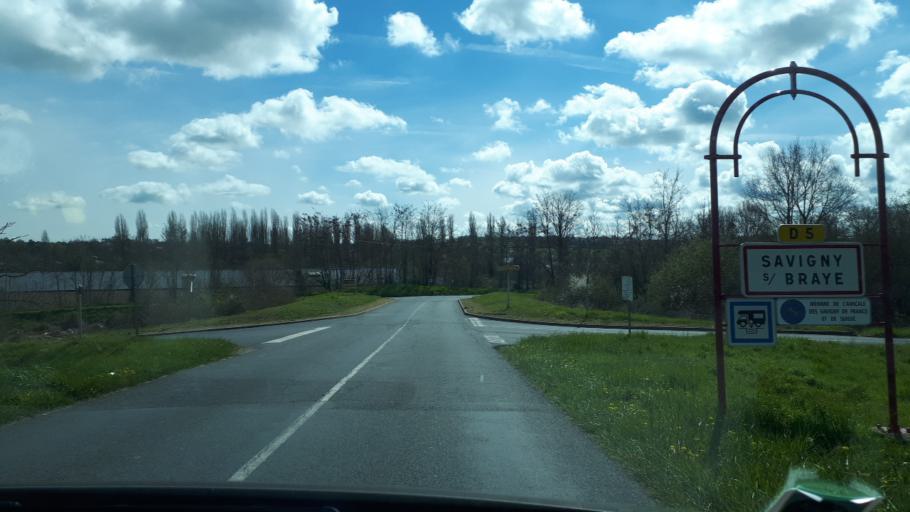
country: FR
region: Centre
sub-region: Departement du Loir-et-Cher
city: Savigny-sur-Braye
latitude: 47.8833
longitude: 0.8000
